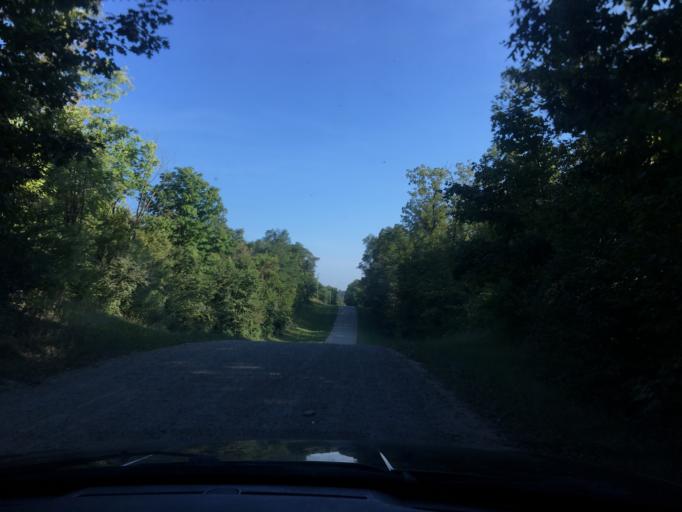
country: US
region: Ohio
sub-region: Logan County
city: West Liberty
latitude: 40.2258
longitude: -83.6616
